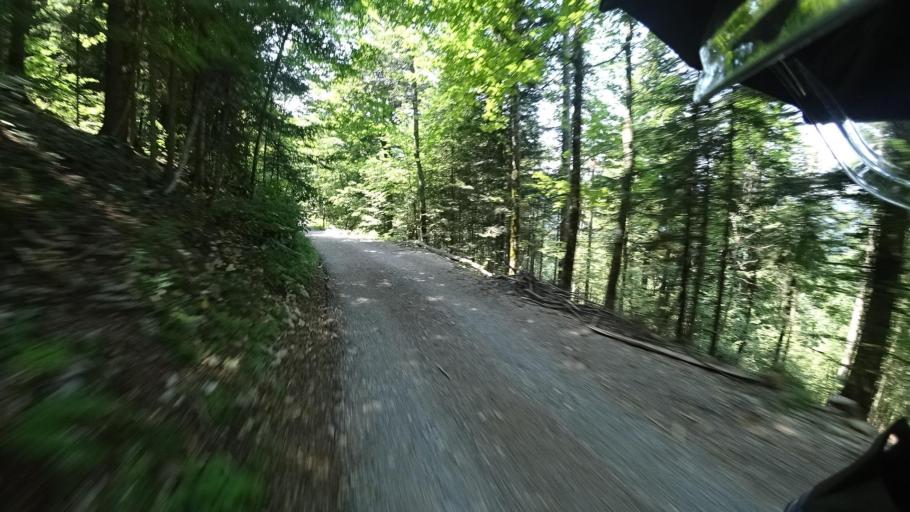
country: HR
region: Primorsko-Goranska
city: Vrbovsko
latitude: 45.3382
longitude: 15.0277
